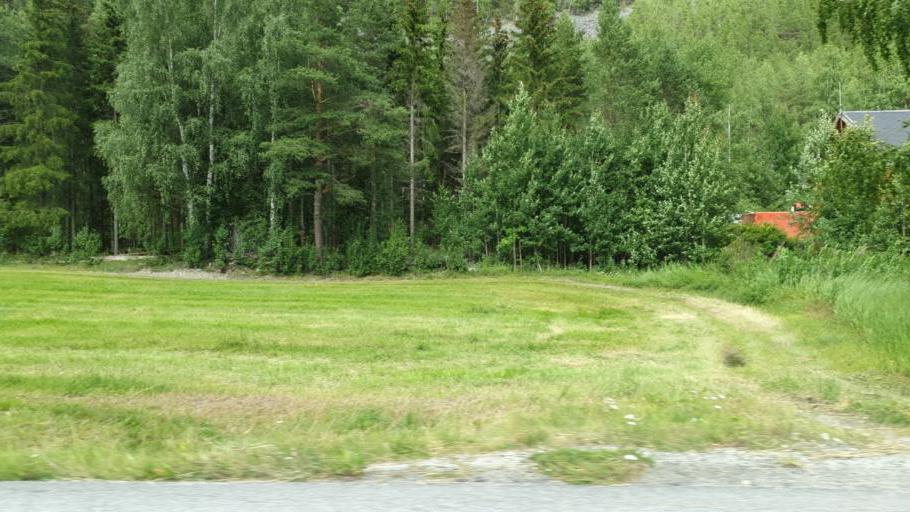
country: NO
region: Oppland
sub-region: Sel
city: Otta
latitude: 61.8436
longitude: 9.3759
